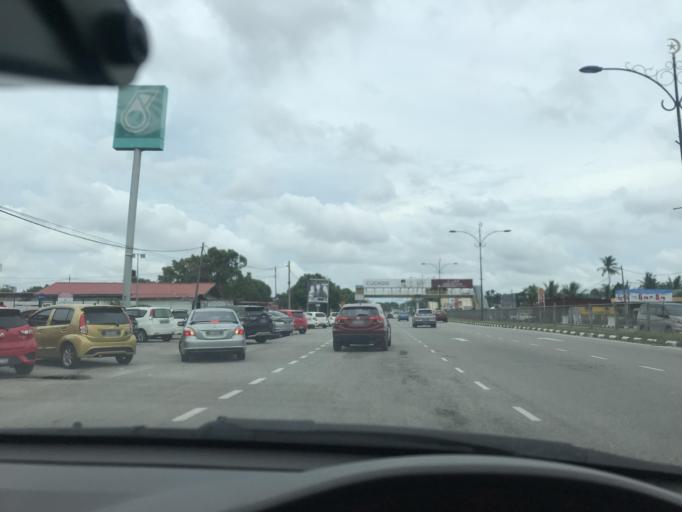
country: MY
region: Kelantan
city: Kota Bharu
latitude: 6.1187
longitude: 102.2187
